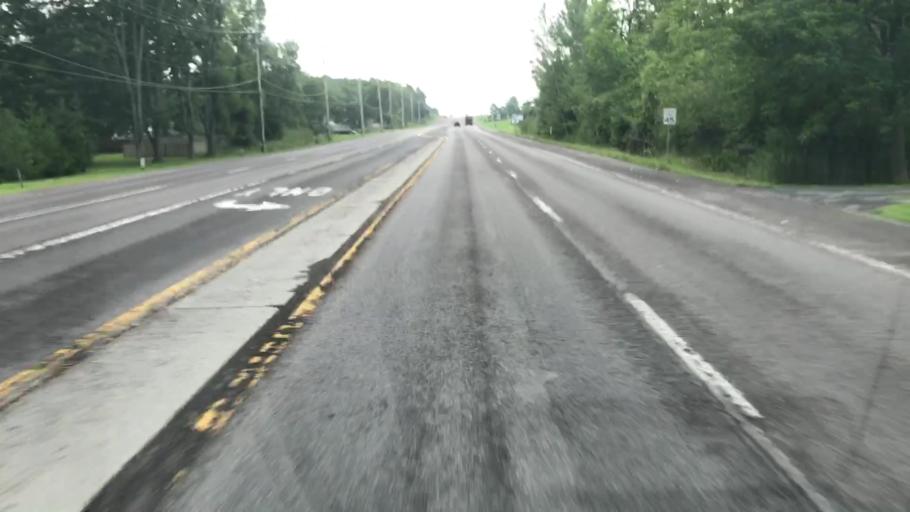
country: US
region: New York
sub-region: Onondaga County
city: Liverpool
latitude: 43.1487
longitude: -76.1882
